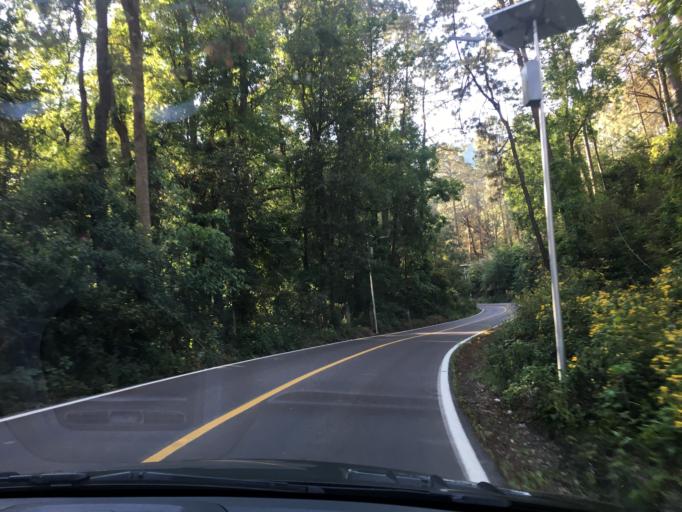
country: MX
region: Mexico
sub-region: Valle de Bravo
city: Casas Viejas
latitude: 19.1449
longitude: -100.1201
